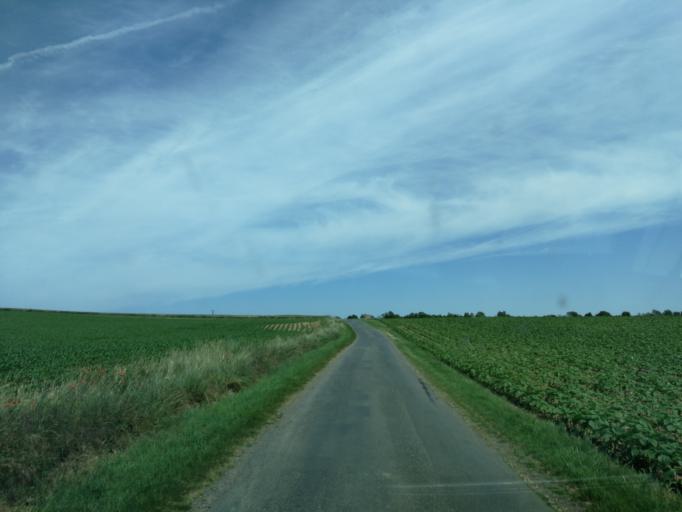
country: FR
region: Pays de la Loire
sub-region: Departement de la Vendee
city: Le Langon
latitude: 46.4237
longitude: -0.8971
